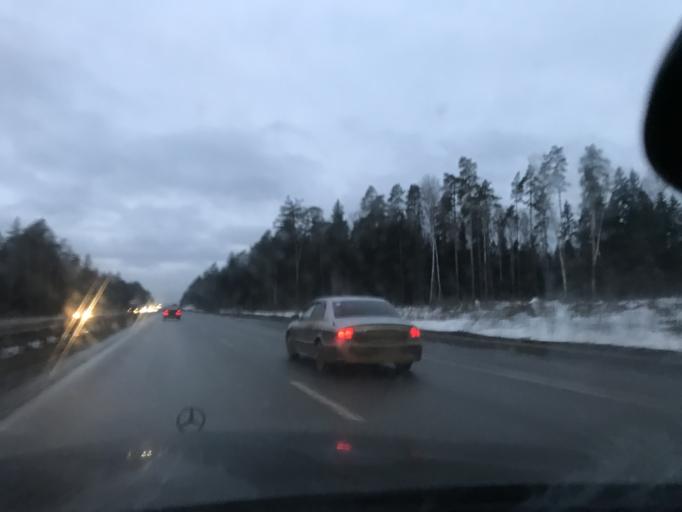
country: RU
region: Vladimir
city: Petushki
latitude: 55.9312
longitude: 39.3692
